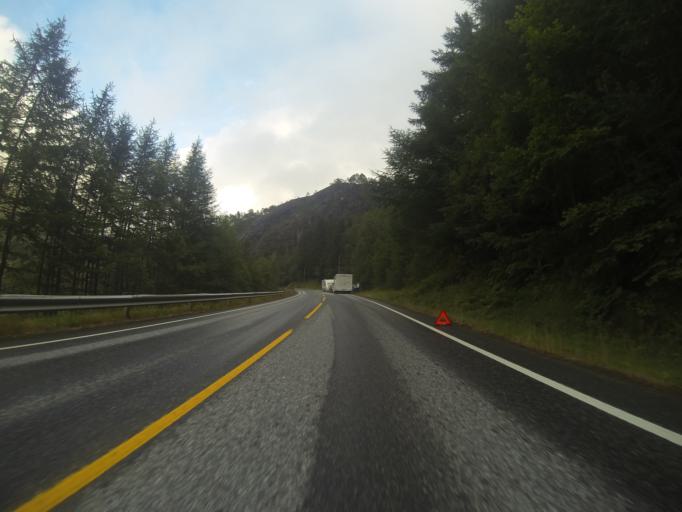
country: NO
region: Rogaland
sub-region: Sauda
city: Sauda
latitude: 59.8744
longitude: 6.3994
